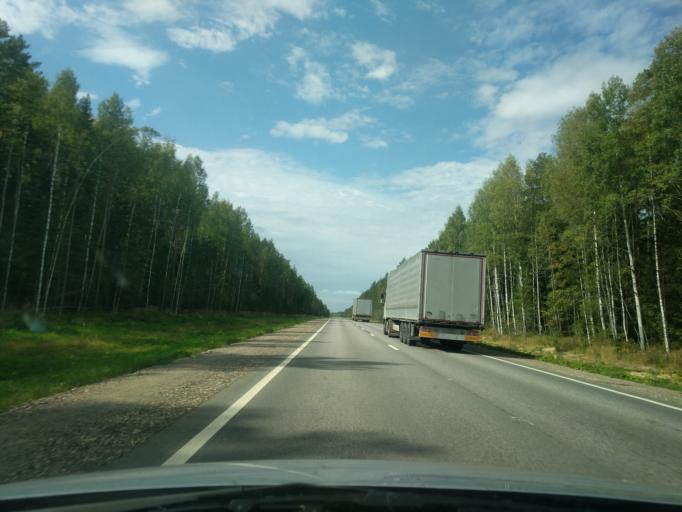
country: RU
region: Kostroma
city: Kadyy
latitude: 57.7983
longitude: 42.8318
